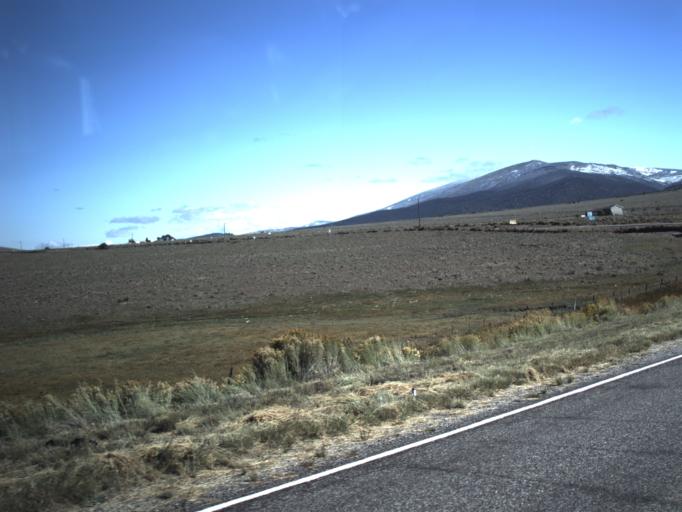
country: US
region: Utah
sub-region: Wayne County
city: Loa
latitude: 38.5674
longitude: -111.8423
